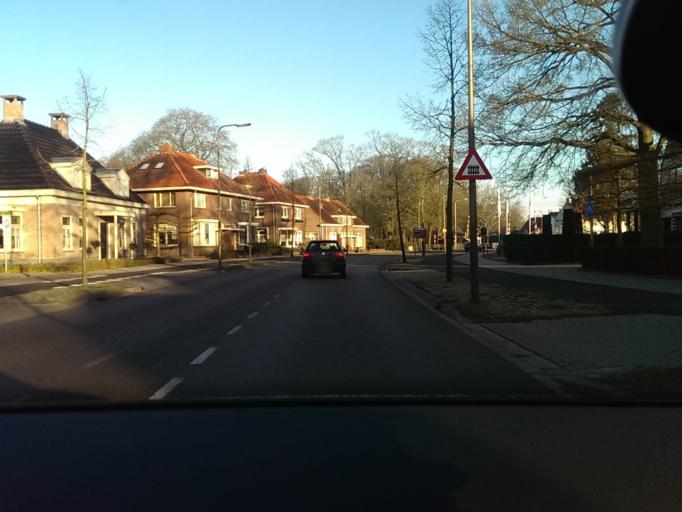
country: NL
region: Overijssel
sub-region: Gemeente Twenterand
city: Den Ham
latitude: 52.5090
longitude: 6.4202
